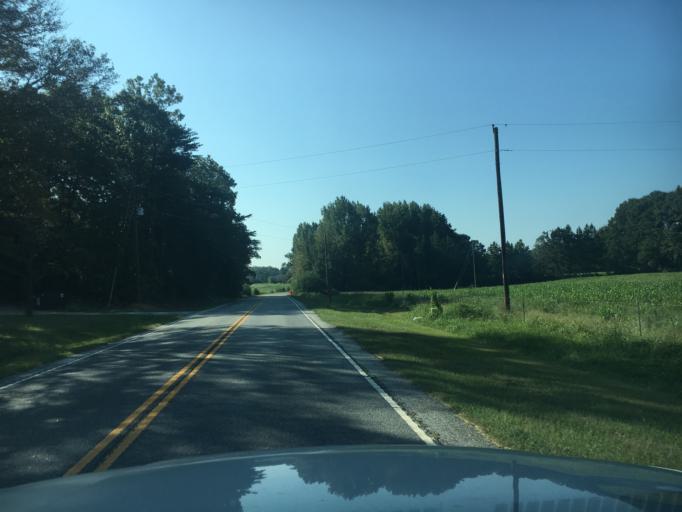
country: US
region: South Carolina
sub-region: Anderson County
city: Williamston
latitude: 34.6129
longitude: -82.3501
